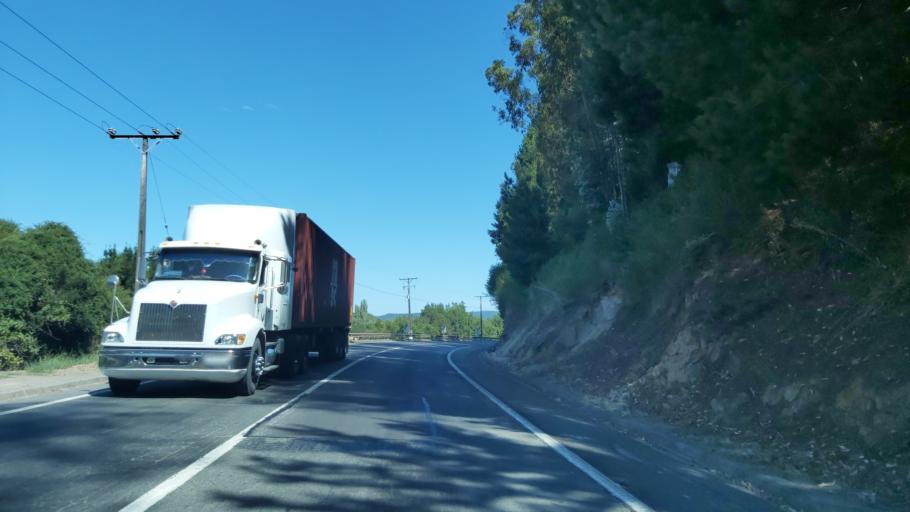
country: CL
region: Biobio
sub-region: Provincia de Concepcion
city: Lota
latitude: -37.1365
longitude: -72.9790
